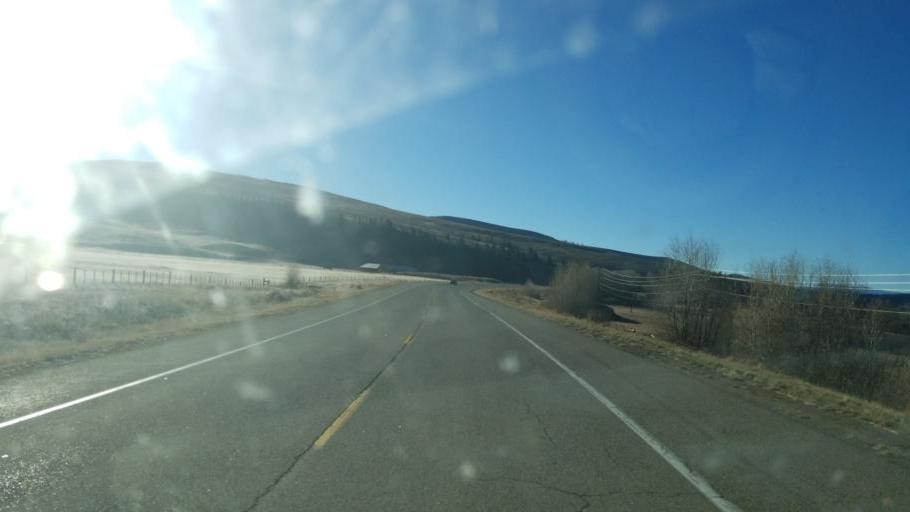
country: US
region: Colorado
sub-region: Gunnison County
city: Gunnison
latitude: 38.7254
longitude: -106.8495
